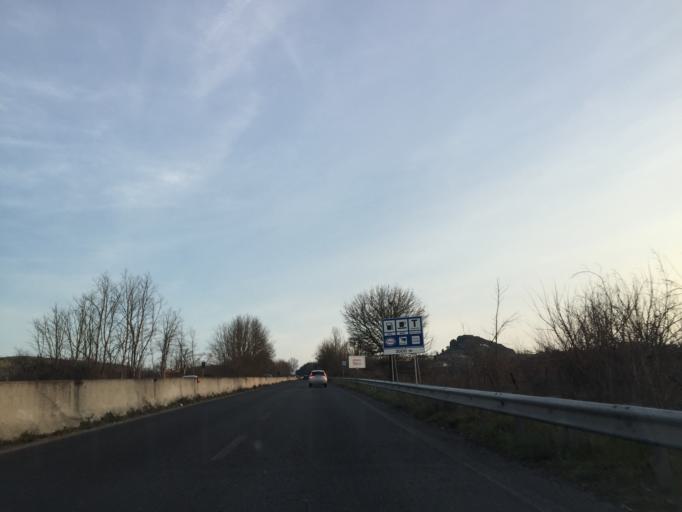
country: IT
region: Latium
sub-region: Citta metropolitana di Roma Capitale
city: Campagnano di Roma
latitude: 42.1426
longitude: 12.3510
